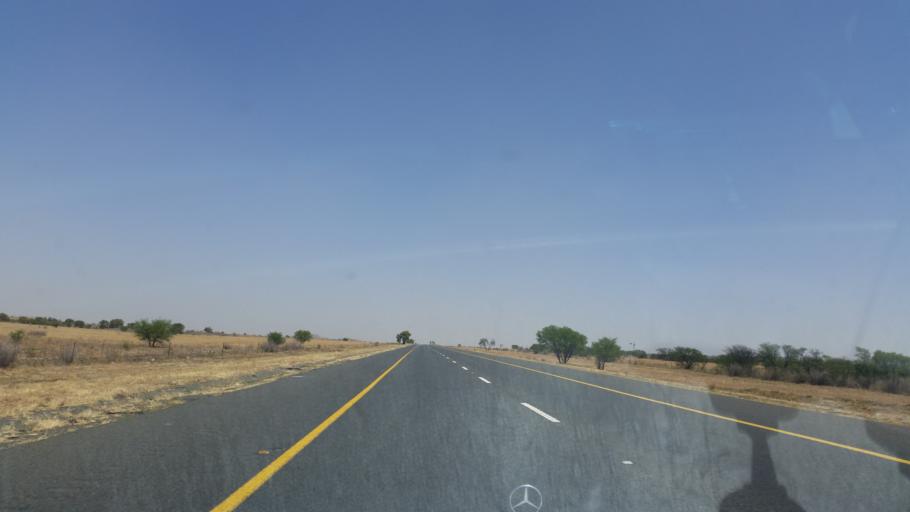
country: ZA
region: Orange Free State
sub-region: Lejweleputswa District Municipality
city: Winburg
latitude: -28.6754
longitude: 26.8379
